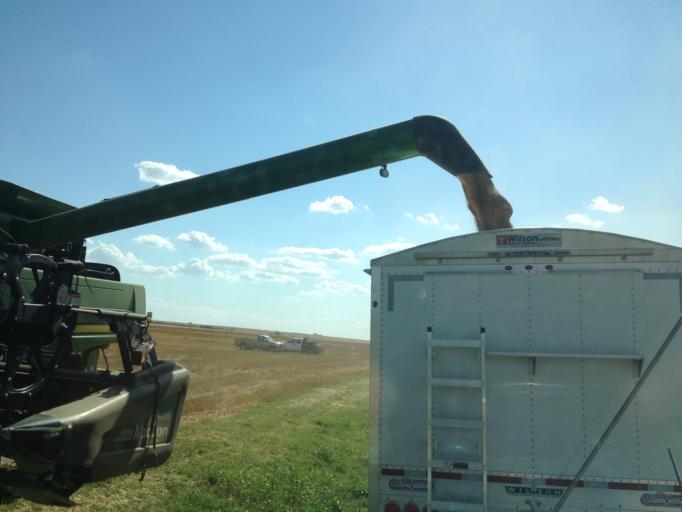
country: US
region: Oklahoma
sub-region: Alfalfa County
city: Helena
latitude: 36.6515
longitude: -98.0423
